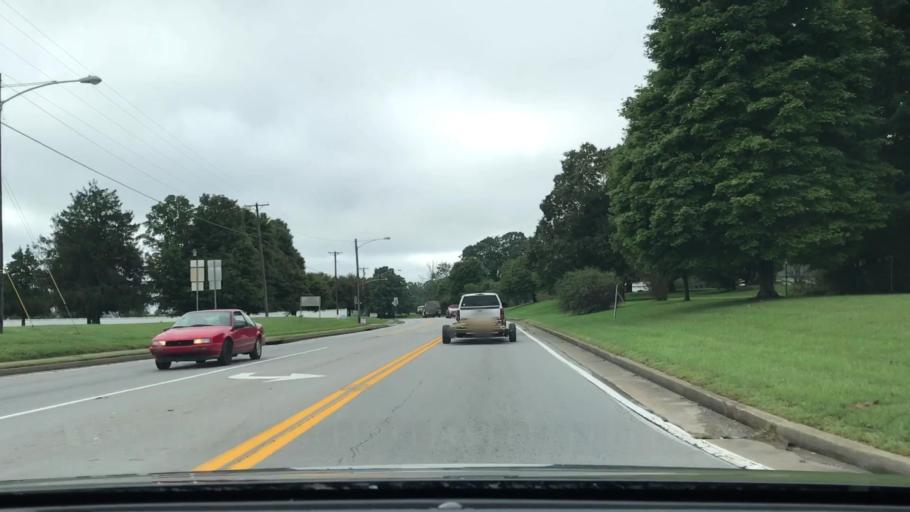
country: US
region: Kentucky
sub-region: Russell County
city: Jamestown
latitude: 36.9983
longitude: -85.0725
